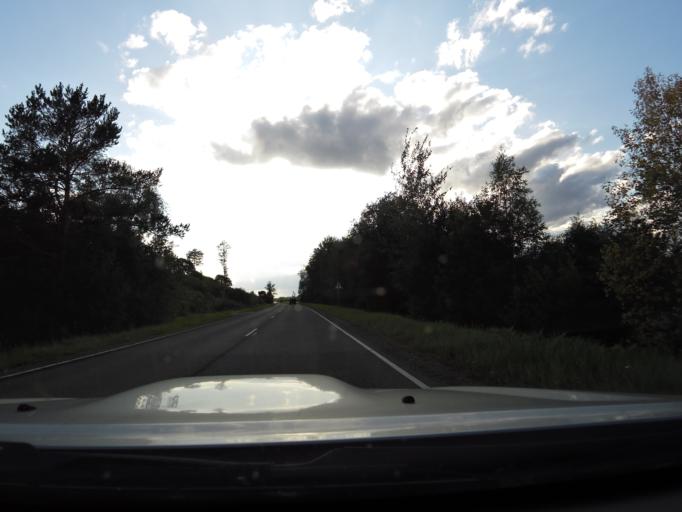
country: LV
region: Nereta
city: Nereta
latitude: 56.1946
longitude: 25.4457
